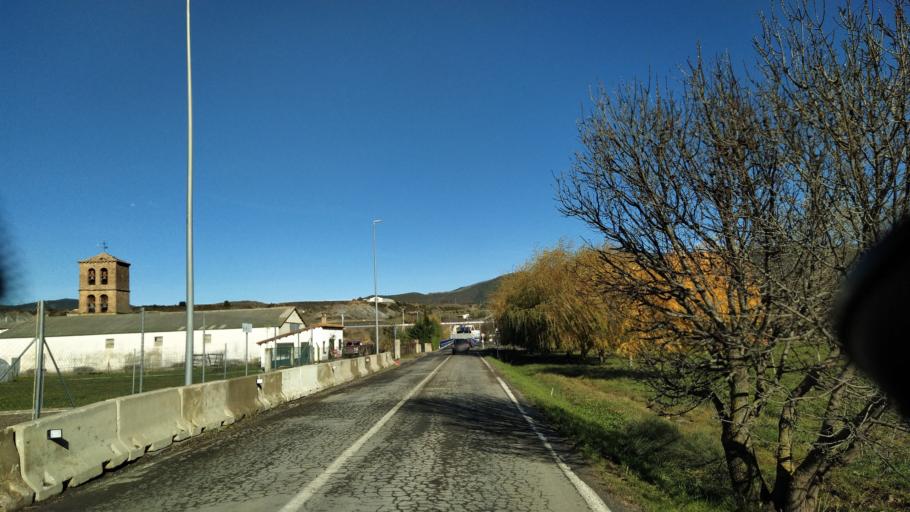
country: ES
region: Aragon
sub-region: Provincia de Huesca
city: Santa Cruz de la Seros
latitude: 42.5603
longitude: -0.7127
